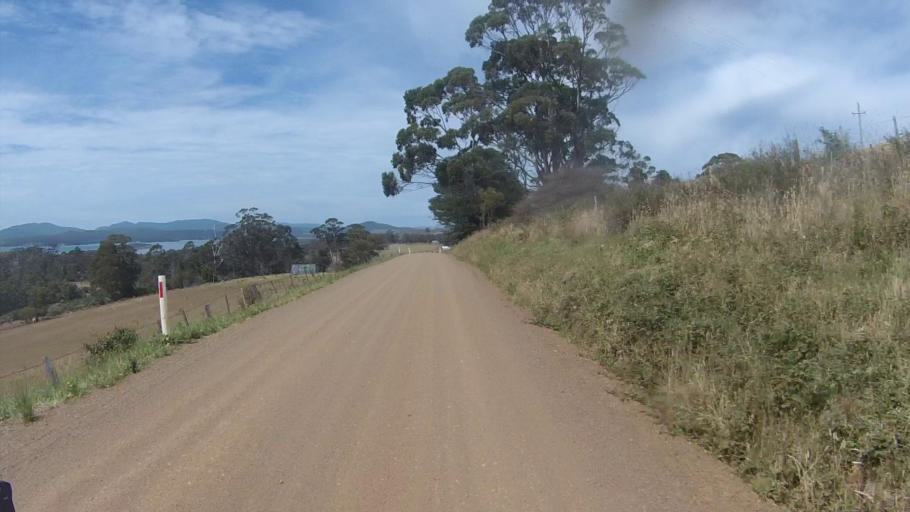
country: AU
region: Tasmania
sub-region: Sorell
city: Sorell
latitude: -42.7941
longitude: 147.8418
